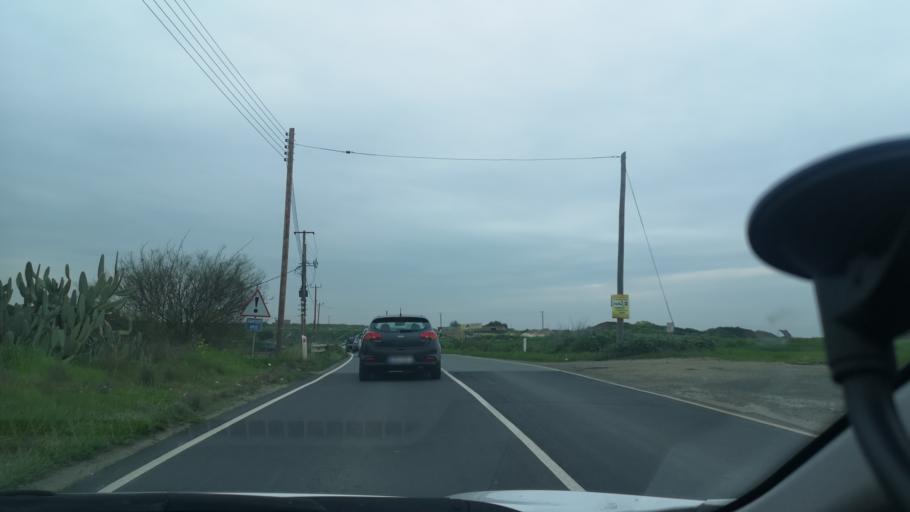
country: CY
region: Lefkosia
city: Tseri
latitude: 35.1026
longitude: 33.3402
